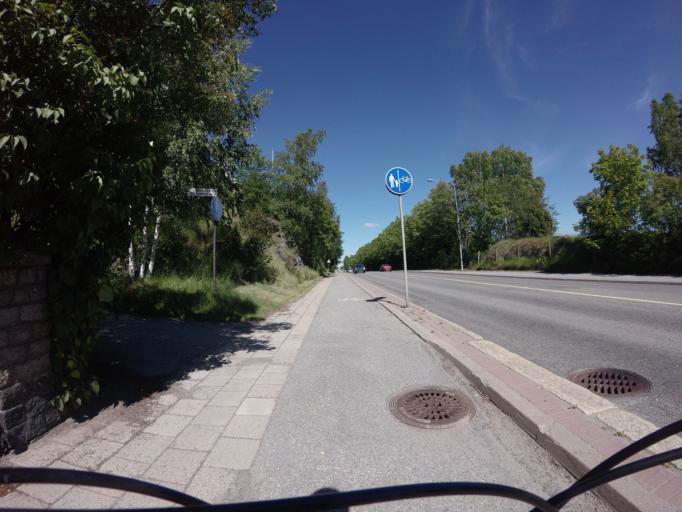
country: FI
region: Varsinais-Suomi
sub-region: Turku
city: Turku
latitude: 60.4565
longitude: 22.2516
